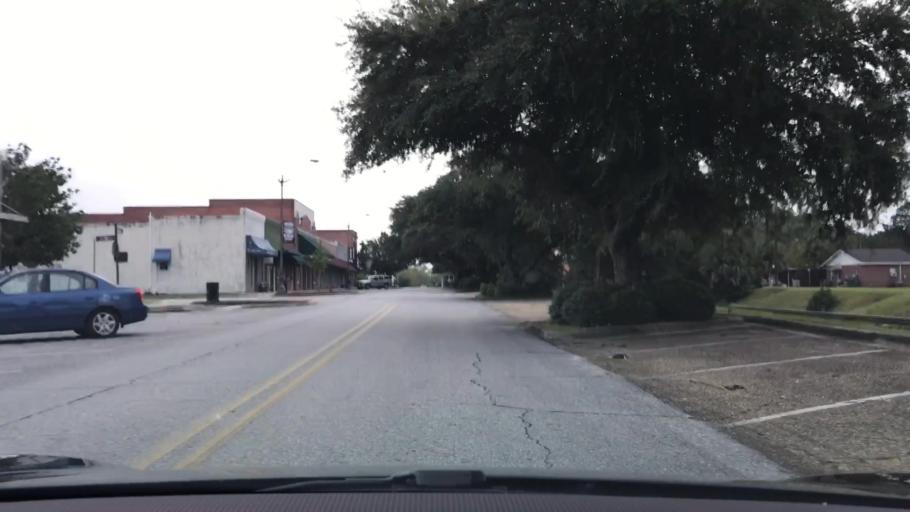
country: US
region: Florida
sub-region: Walton County
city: DeFuniak Springs
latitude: 30.7204
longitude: -86.1160
